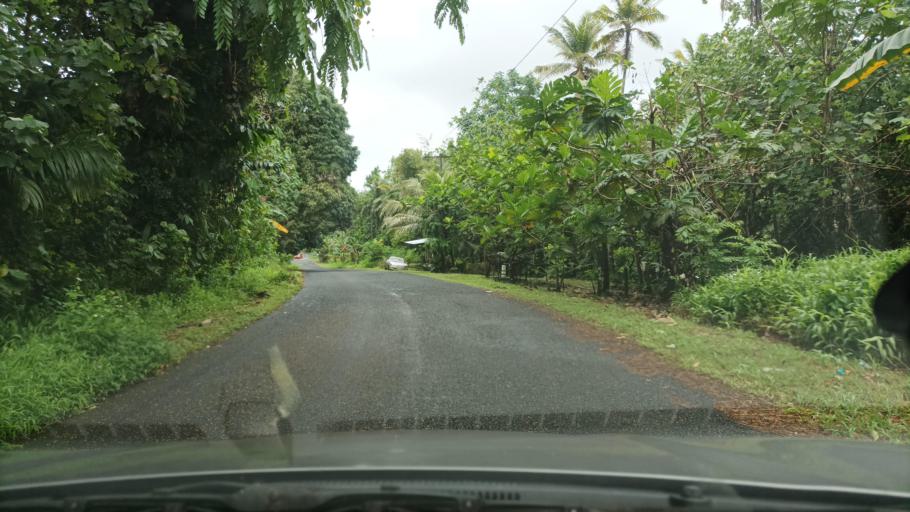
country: FM
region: Pohnpei
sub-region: Madolenihm Municipality
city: Madolenihm Municipality Government
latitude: 6.8445
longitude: 158.3022
